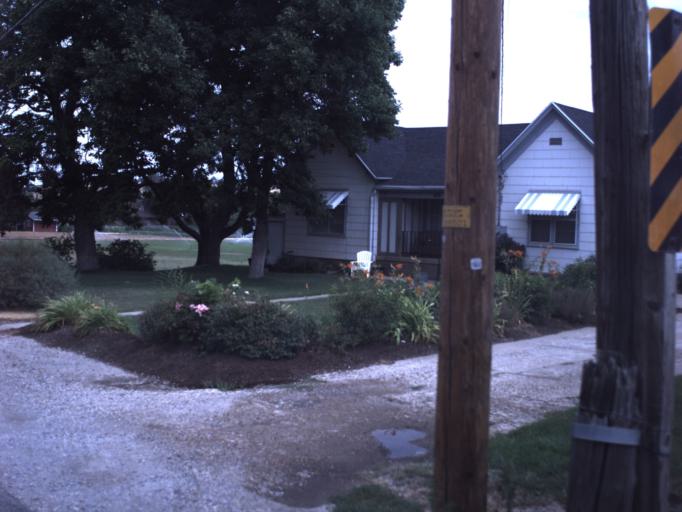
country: US
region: Utah
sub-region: Davis County
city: Hill Air Force Bace
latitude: 41.1407
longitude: -111.9713
